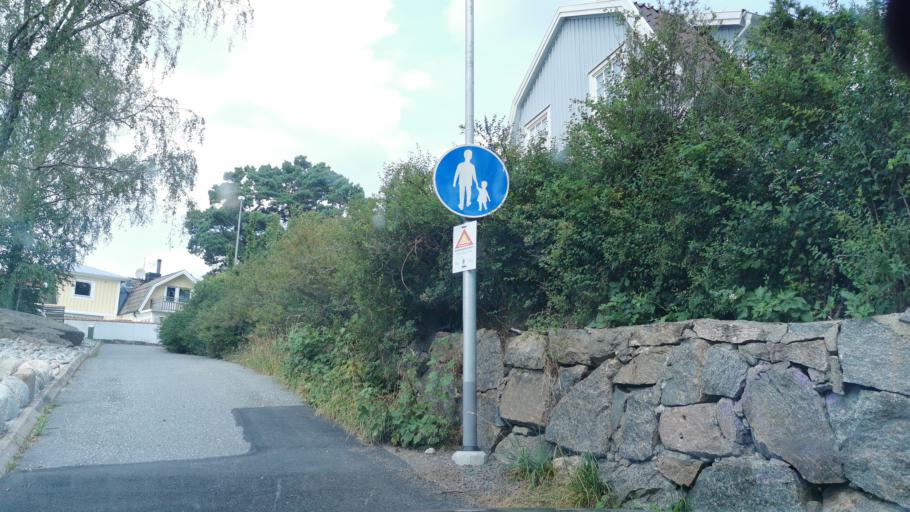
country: SE
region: Vaestra Goetaland
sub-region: Molndal
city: Moelndal
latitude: 57.6745
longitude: 11.9851
